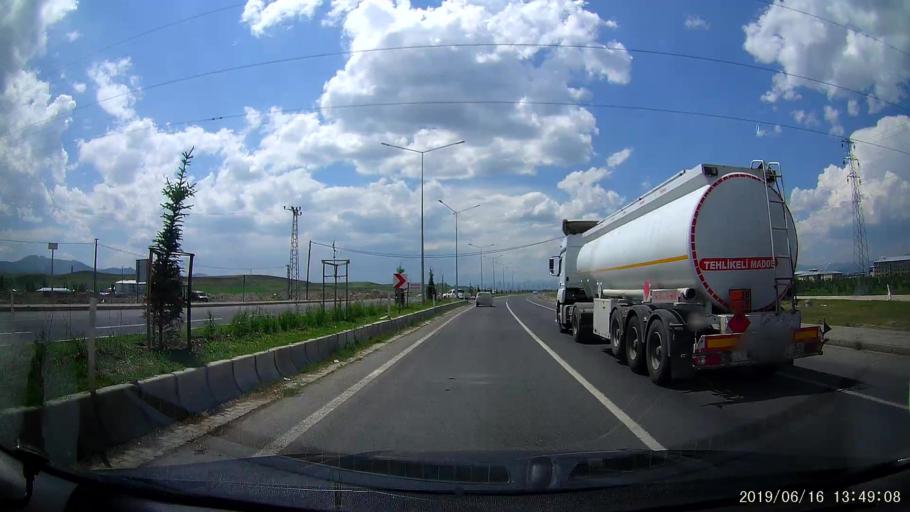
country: TR
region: Agri
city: Agri
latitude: 39.7153
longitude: 42.9950
